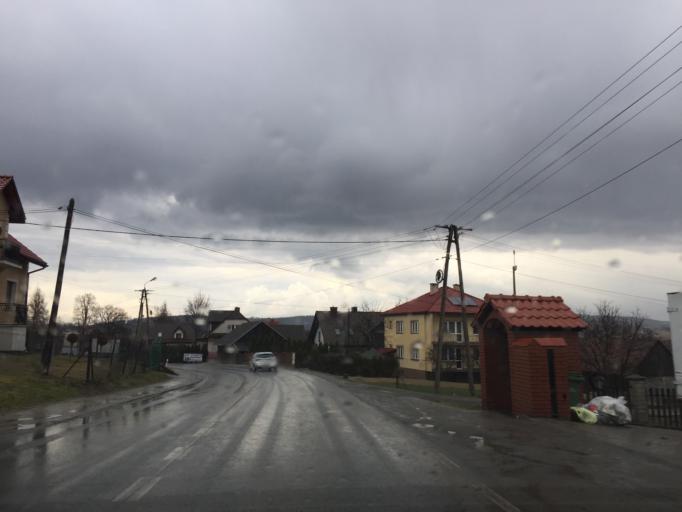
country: PL
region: Lesser Poland Voivodeship
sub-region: Powiat myslenicki
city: Sulkowice
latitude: 49.8335
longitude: 19.7966
